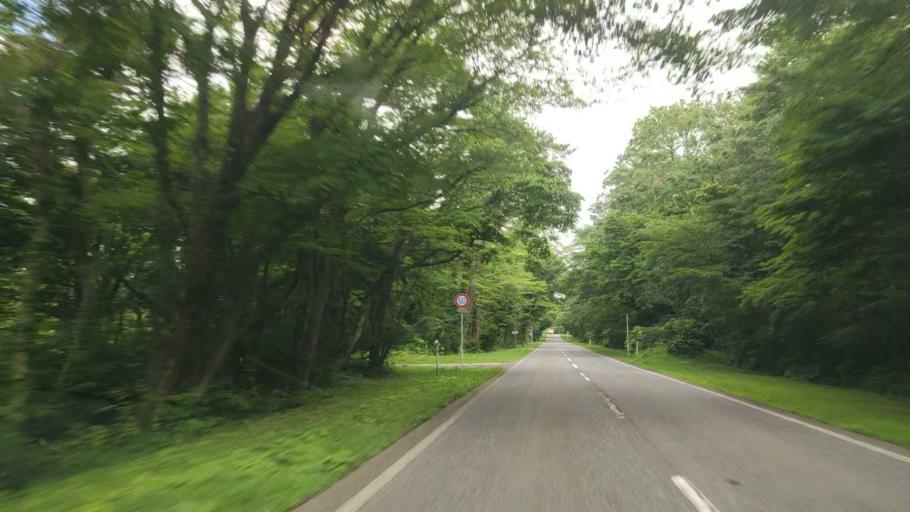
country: JP
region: Tottori
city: Yonago
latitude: 35.4003
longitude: 133.4968
